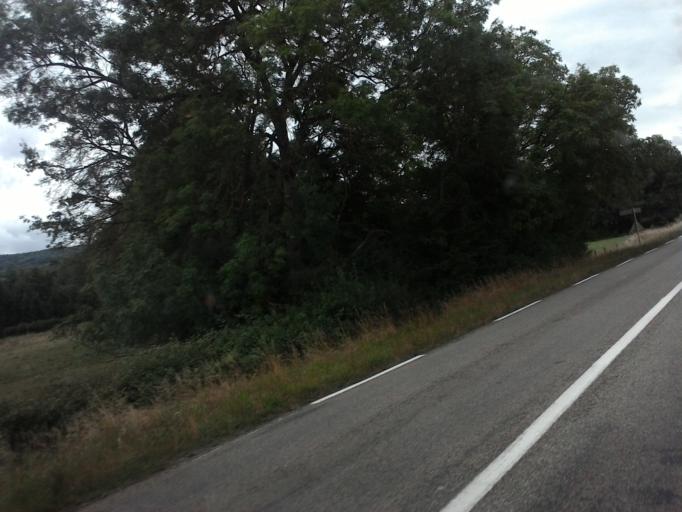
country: FR
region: Franche-Comte
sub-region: Departement du Jura
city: Cousance
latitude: 46.5929
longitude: 5.4530
